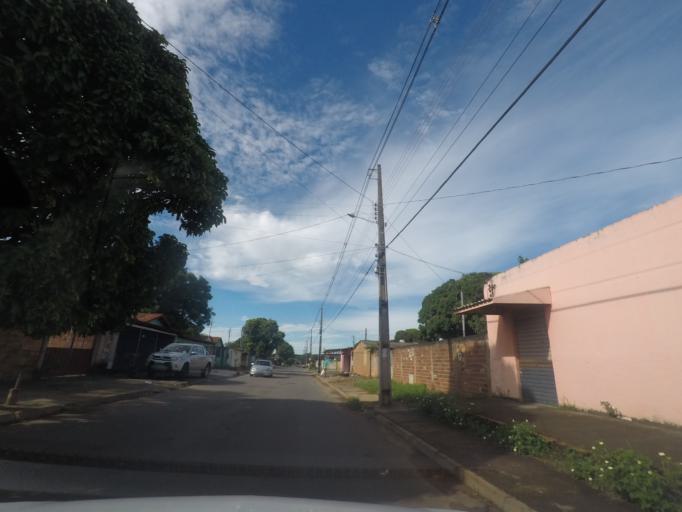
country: BR
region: Goias
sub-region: Aparecida De Goiania
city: Aparecida de Goiania
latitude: -16.8216
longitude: -49.2955
